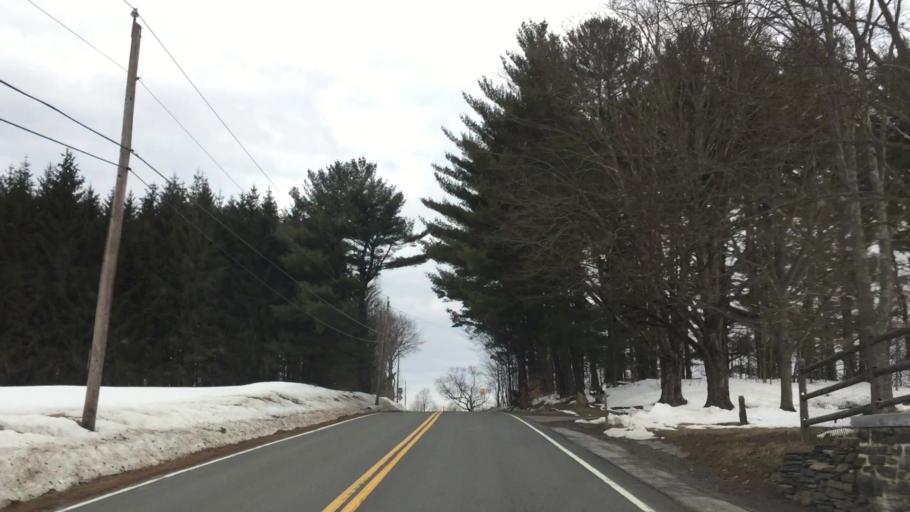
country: US
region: Massachusetts
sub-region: Berkshire County
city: Hinsdale
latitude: 42.4207
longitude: -73.0747
